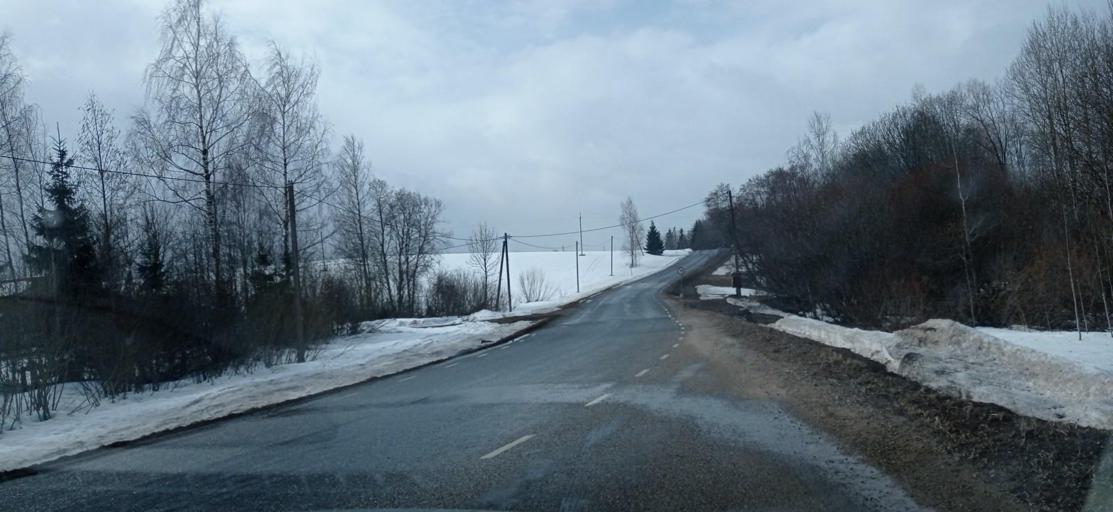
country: EE
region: Tartu
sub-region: Noo vald
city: Noo
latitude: 58.0870
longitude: 26.6561
